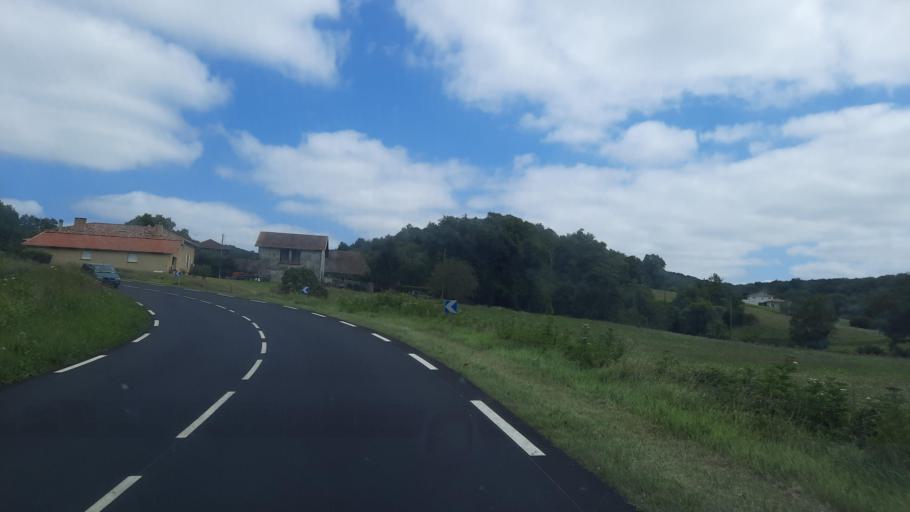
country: FR
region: Midi-Pyrenees
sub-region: Departement de la Haute-Garonne
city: Boulogne-sur-Gesse
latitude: 43.2855
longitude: 0.5450
